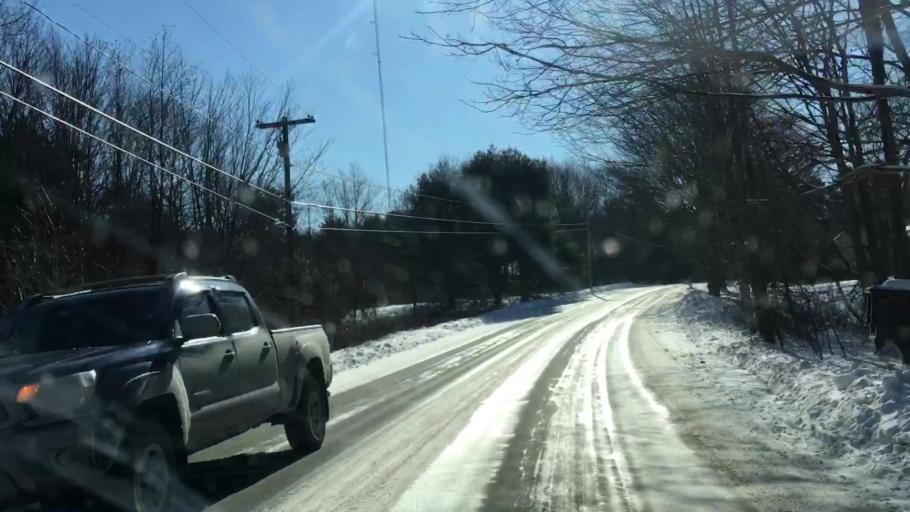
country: US
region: Maine
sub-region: Cumberland County
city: Brunswick
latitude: 43.8975
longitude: -69.9984
